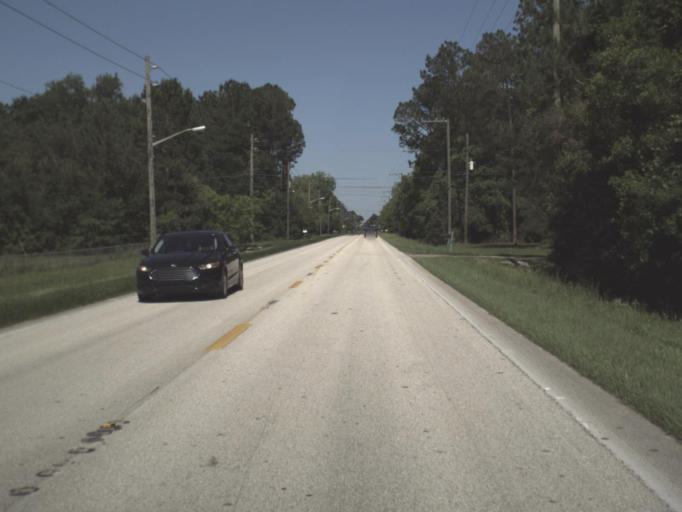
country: US
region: Florida
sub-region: Duval County
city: Baldwin
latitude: 30.3028
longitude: -82.0144
